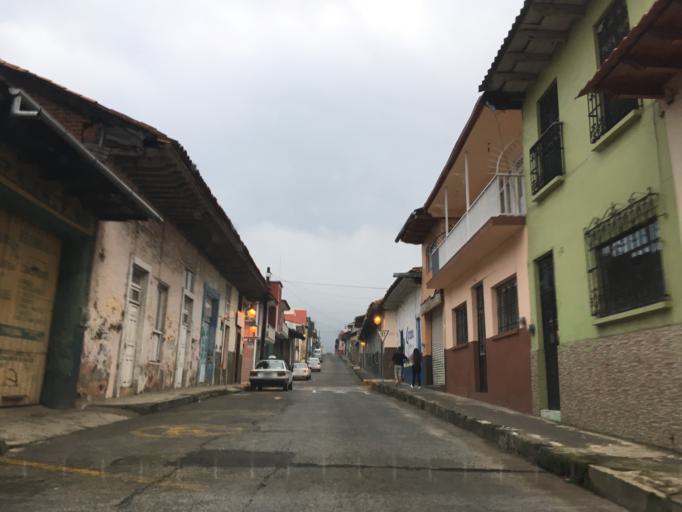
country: MX
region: Michoacan
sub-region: Uruapan
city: Uruapan
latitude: 19.4209
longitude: -102.0671
